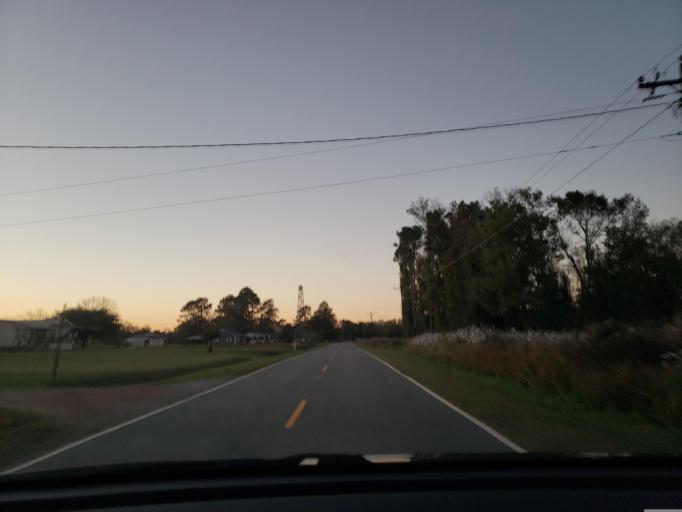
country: US
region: North Carolina
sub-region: Duplin County
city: Beulaville
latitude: 34.7901
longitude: -77.7619
